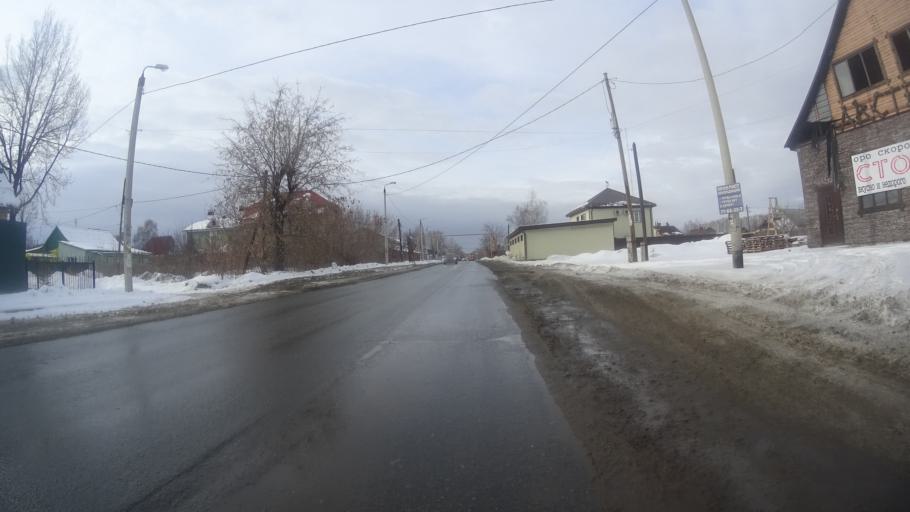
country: RU
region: Chelyabinsk
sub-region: Gorod Chelyabinsk
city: Chelyabinsk
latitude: 55.1306
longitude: 61.3880
